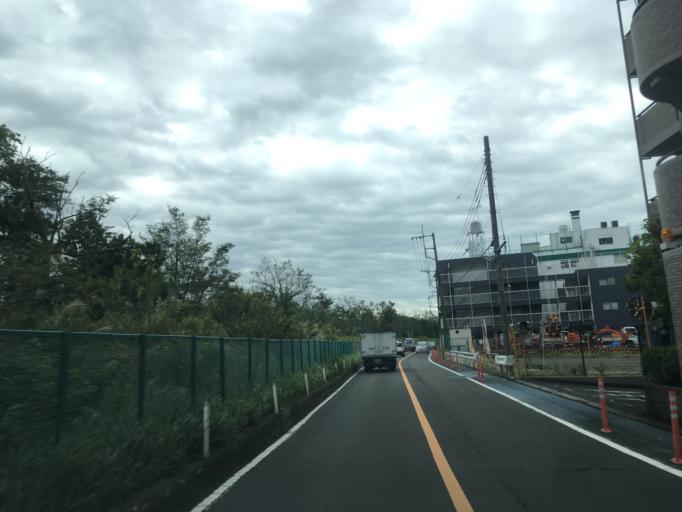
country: JP
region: Tokyo
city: Chofugaoka
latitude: 35.6496
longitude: 139.5142
